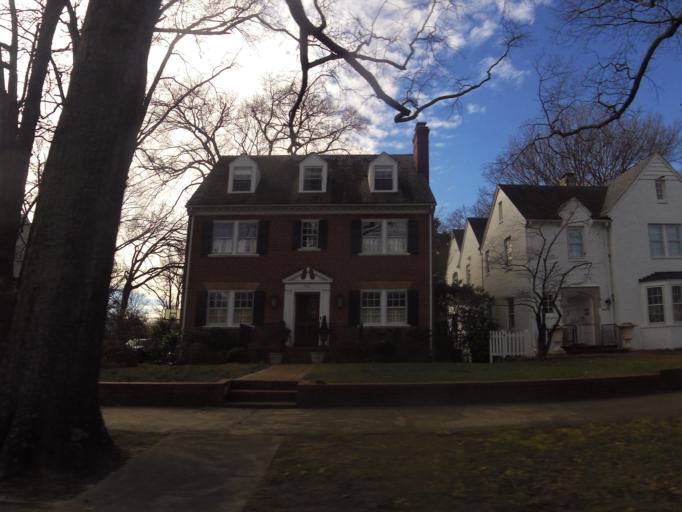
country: US
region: Virginia
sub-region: Henrico County
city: Dumbarton
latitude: 37.5724
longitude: -77.4915
